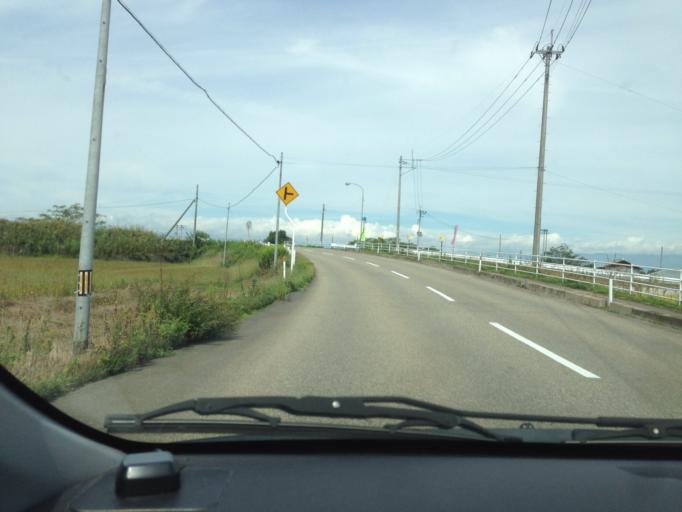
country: JP
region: Fukushima
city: Kitakata
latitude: 37.5477
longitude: 139.8556
